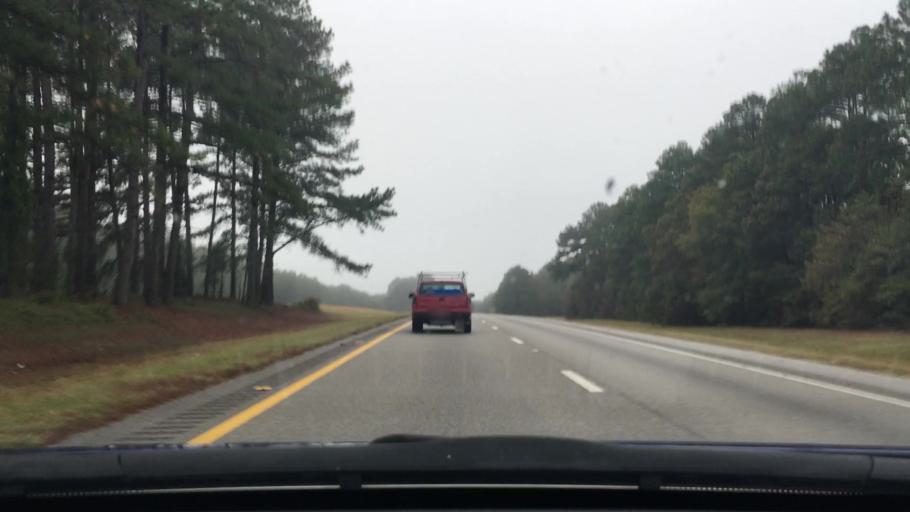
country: US
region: South Carolina
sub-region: Kershaw County
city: Camden
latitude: 34.2090
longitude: -80.4645
